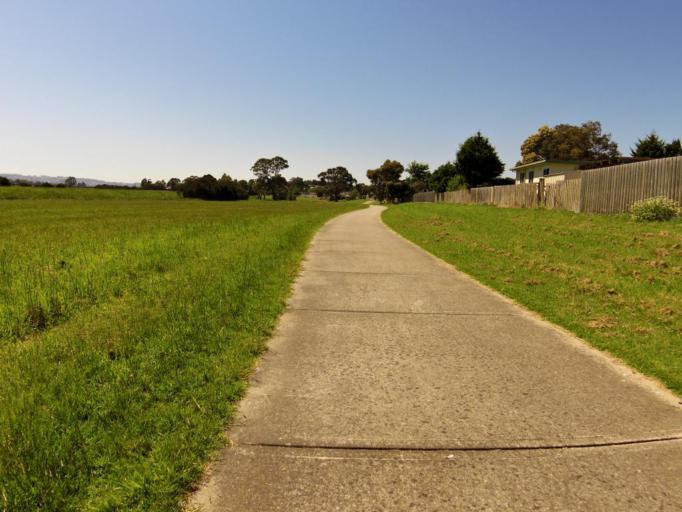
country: AU
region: Victoria
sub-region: Casey
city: Hallam
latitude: -38.0208
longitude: 145.2552
